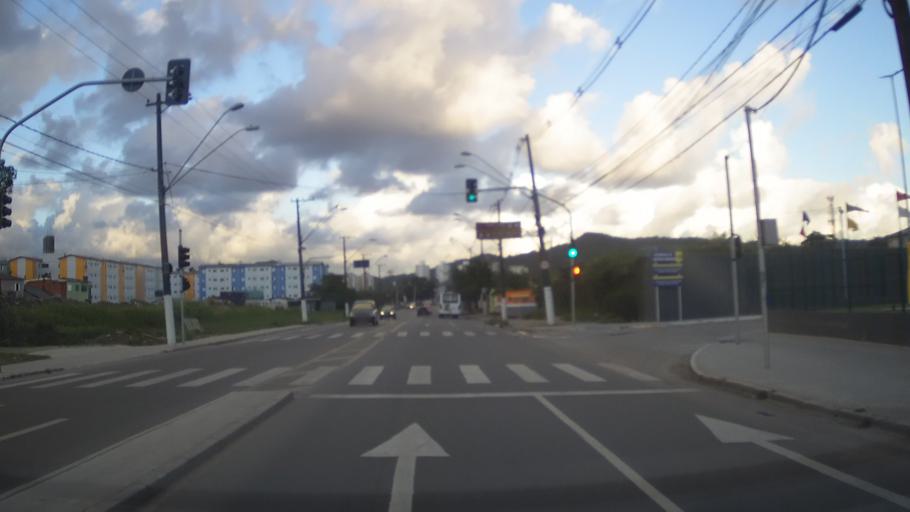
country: BR
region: Sao Paulo
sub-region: Sao Vicente
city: Sao Vicente
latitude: -23.9502
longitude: -46.3894
